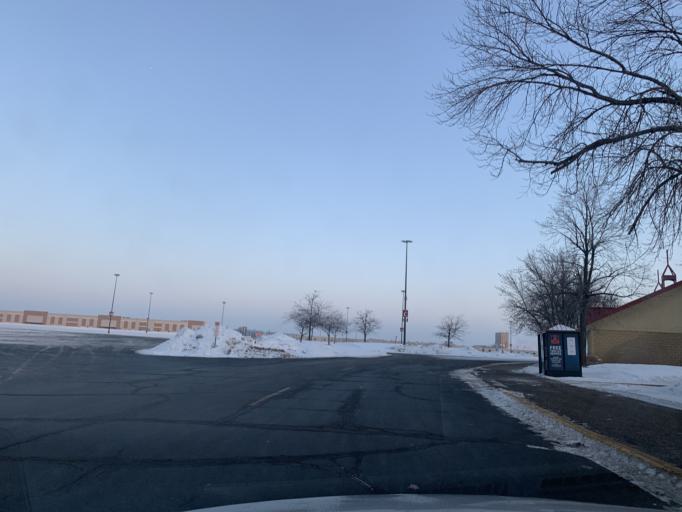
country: US
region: Minnesota
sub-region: Scott County
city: Shakopee
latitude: 44.7907
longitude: -93.4847
